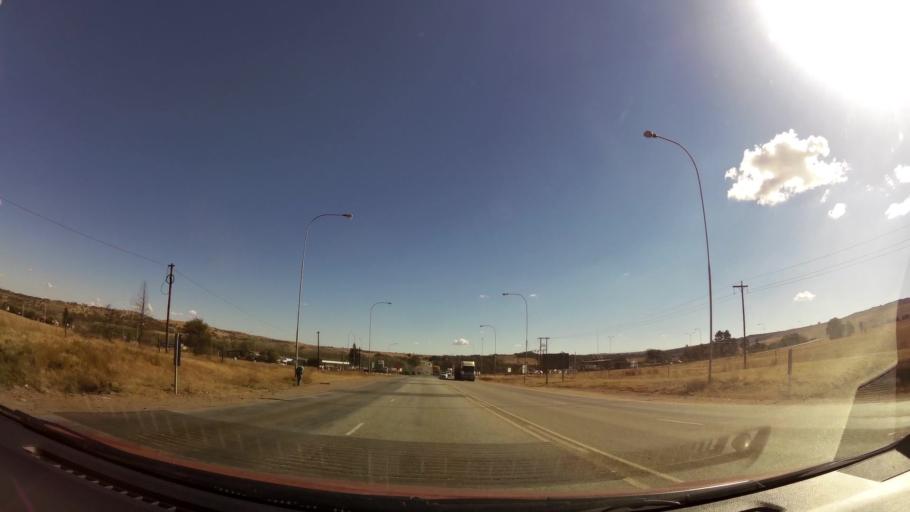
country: ZA
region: North-West
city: Fochville
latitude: -26.4412
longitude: 27.4851
